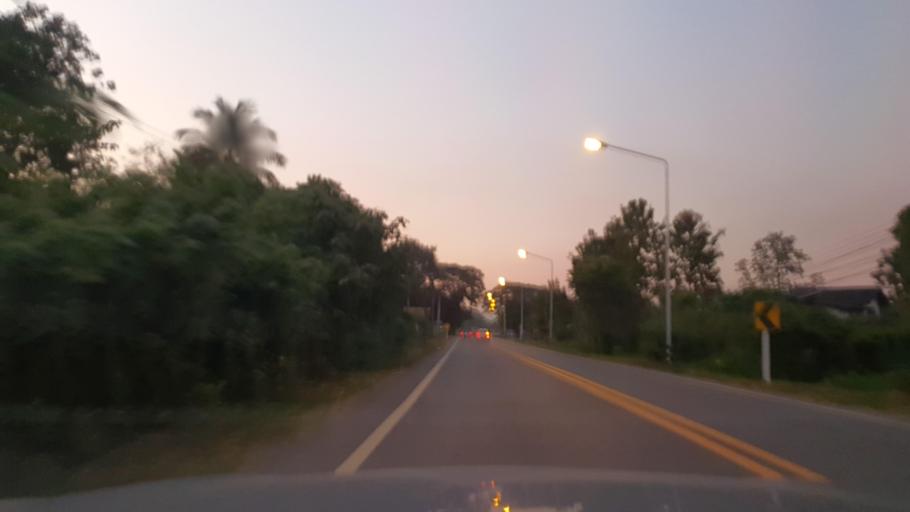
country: TH
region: Phayao
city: Dok Kham Tai
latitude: 19.1509
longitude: 99.9980
